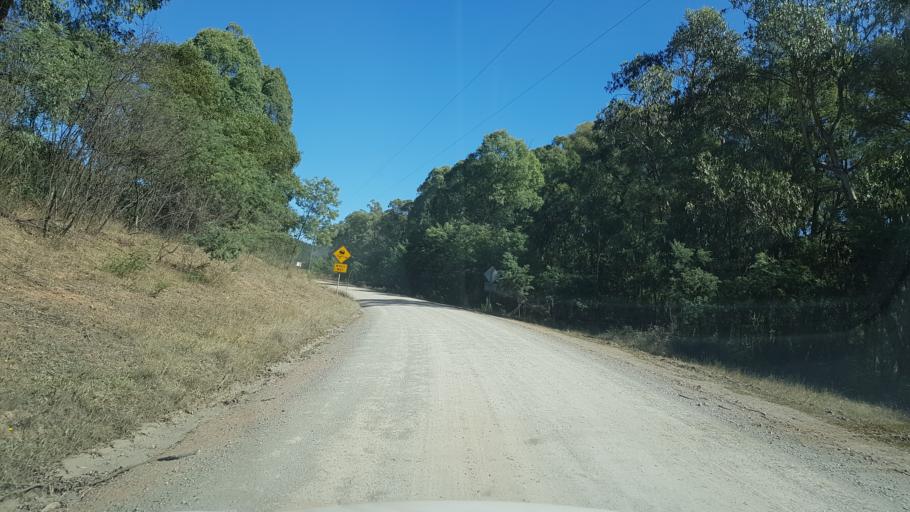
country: AU
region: Victoria
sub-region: Mansfield
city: Mansfield
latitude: -36.8522
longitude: 146.5203
